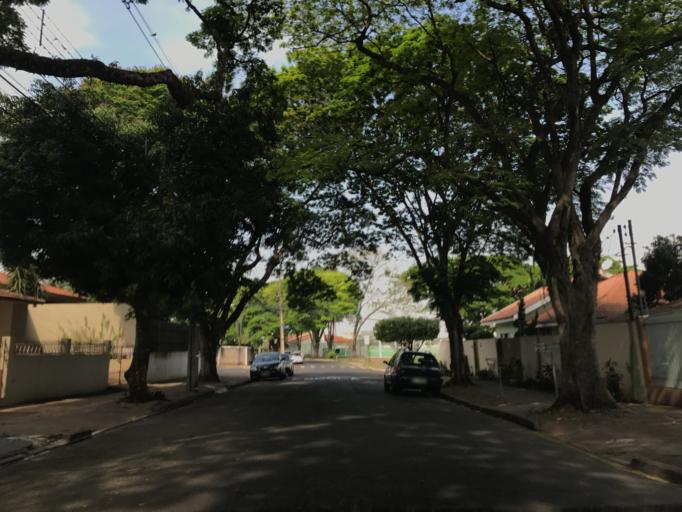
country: BR
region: Parana
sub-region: Maringa
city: Maringa
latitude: -23.4367
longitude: -51.9505
